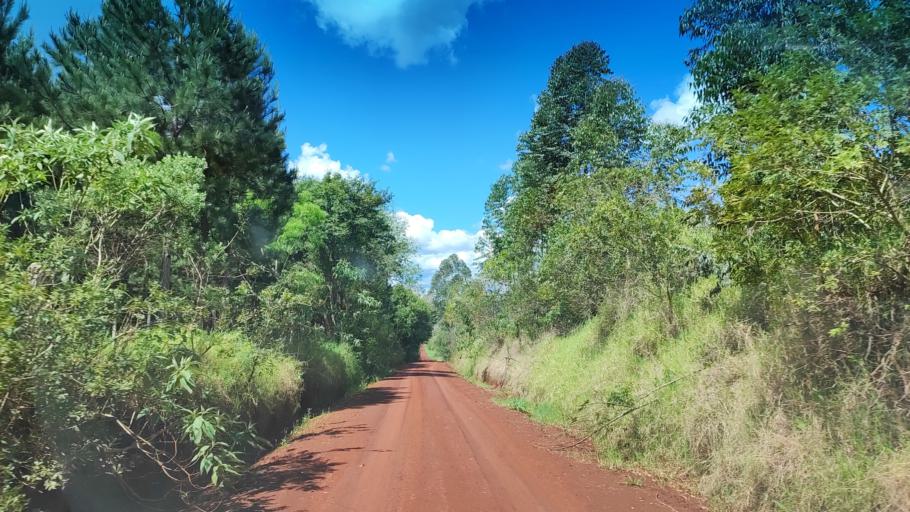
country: AR
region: Misiones
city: Capiovi
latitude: -26.9528
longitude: -55.0430
